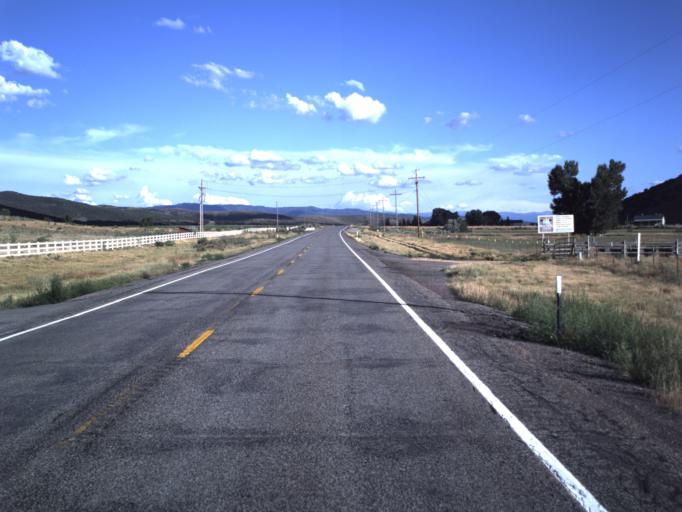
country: US
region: Utah
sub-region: Utah County
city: Woodland Hills
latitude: 39.8738
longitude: -111.5380
